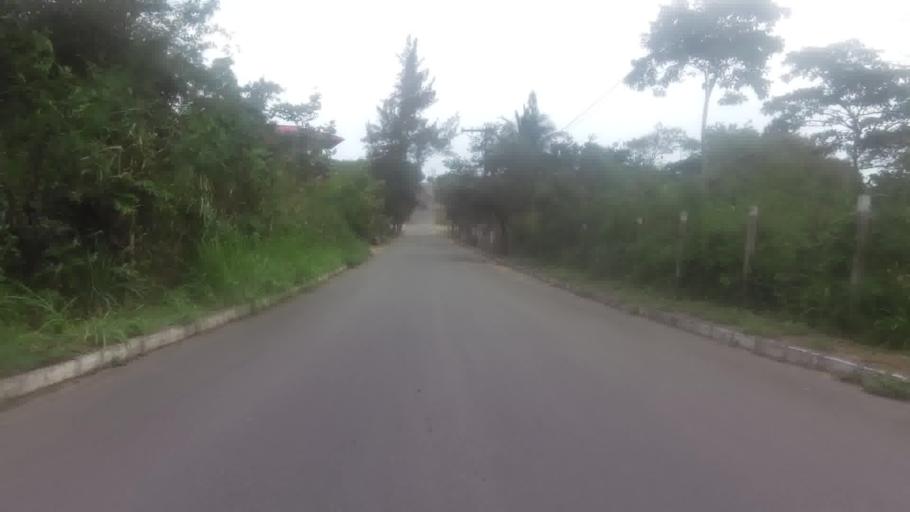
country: BR
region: Espirito Santo
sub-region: Piuma
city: Piuma
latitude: -20.7995
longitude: -40.5866
